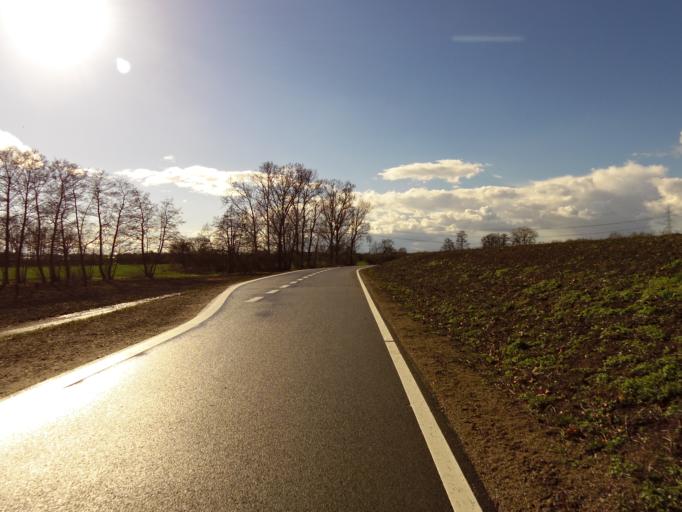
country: DE
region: Hesse
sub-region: Regierungsbezirk Darmstadt
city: Biblis
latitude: 49.6761
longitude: 8.4271
